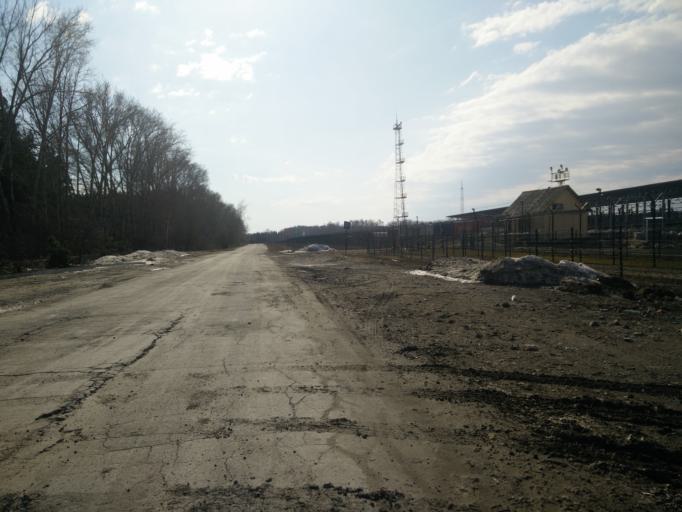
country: RU
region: Novosibirsk
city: Berdsk
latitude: 54.7636
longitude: 83.0780
